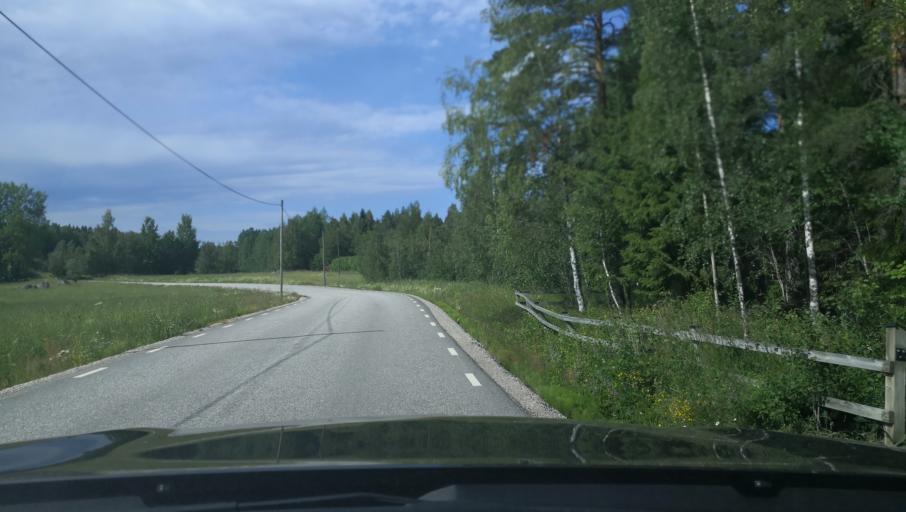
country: SE
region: Vaestmanland
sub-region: Norbergs Kommun
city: Norberg
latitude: 59.9727
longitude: 15.9697
